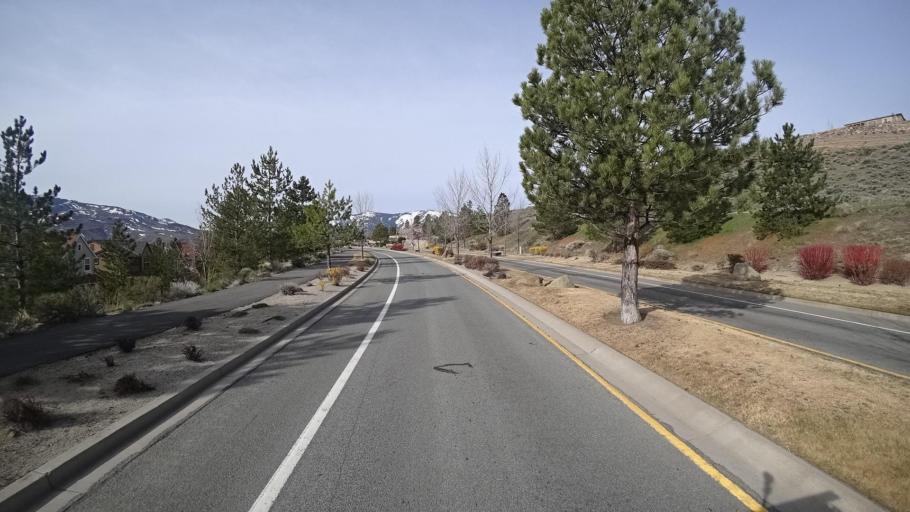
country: US
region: Nevada
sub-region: Washoe County
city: Mogul
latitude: 39.5356
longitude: -119.9495
